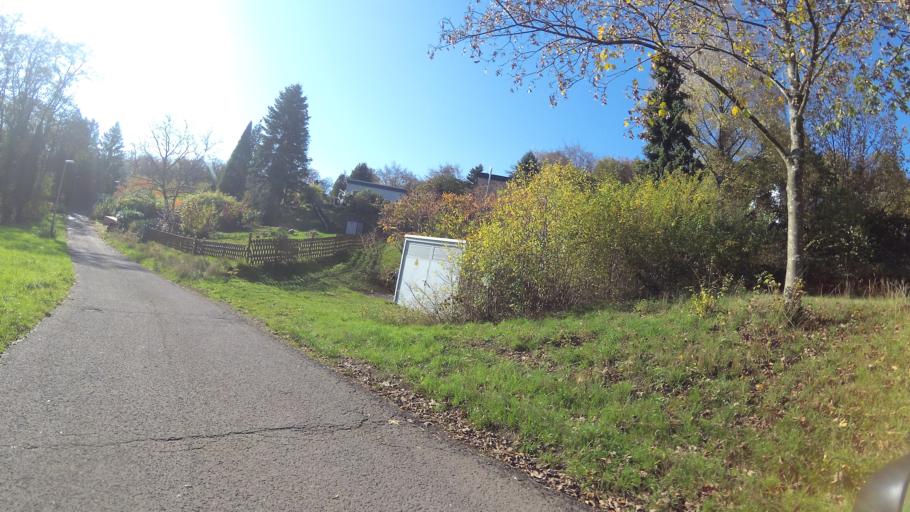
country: DE
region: Saarland
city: Losheim
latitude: 49.5430
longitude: 6.7736
